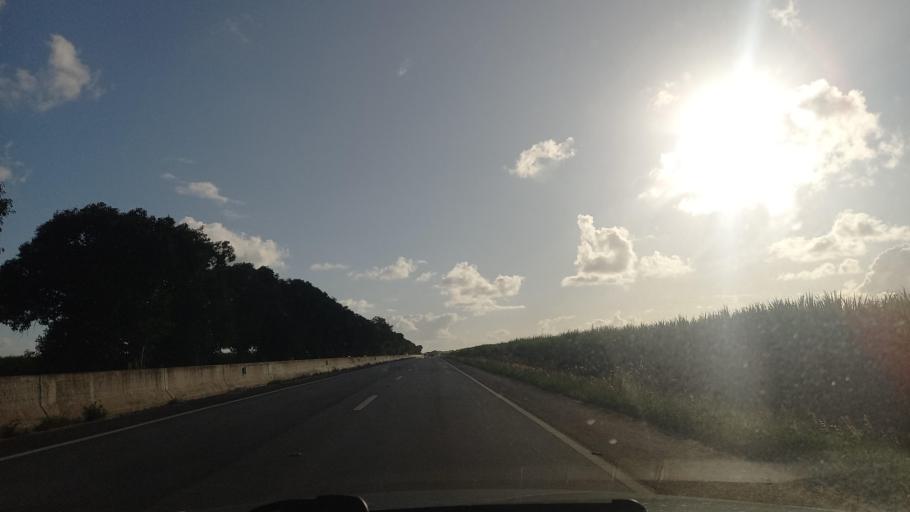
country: BR
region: Alagoas
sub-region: Sao Miguel Dos Campos
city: Sao Miguel dos Campos
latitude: -9.8001
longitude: -36.1722
